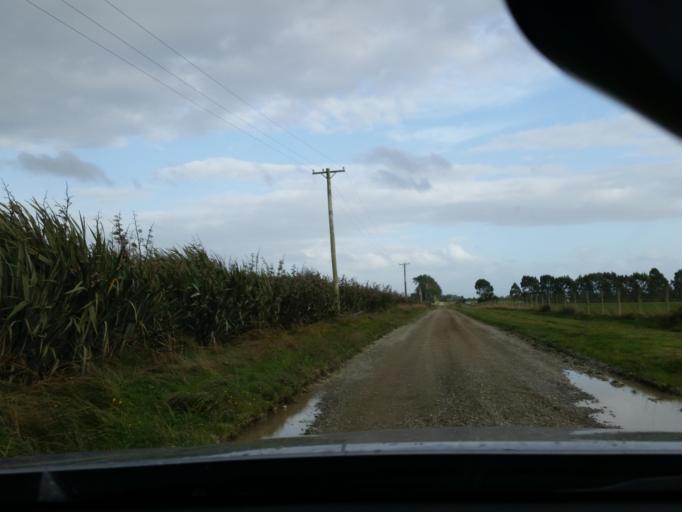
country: NZ
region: Southland
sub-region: Southland District
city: Winton
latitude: -46.2522
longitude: 168.3212
